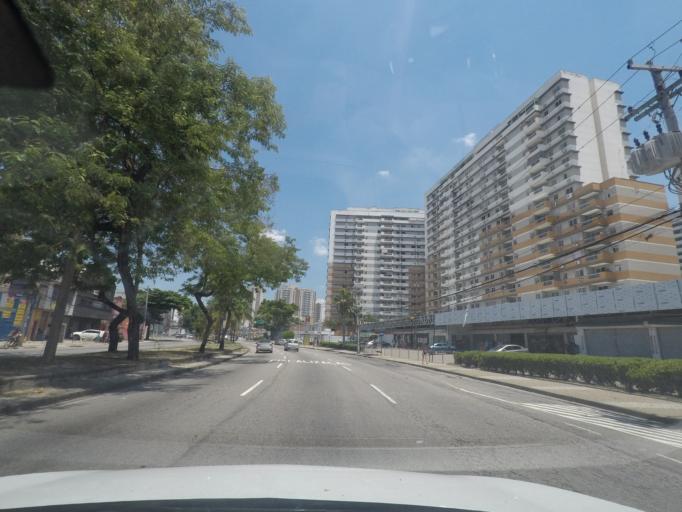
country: BR
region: Rio de Janeiro
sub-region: Rio De Janeiro
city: Rio de Janeiro
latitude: -22.8852
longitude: -43.2903
